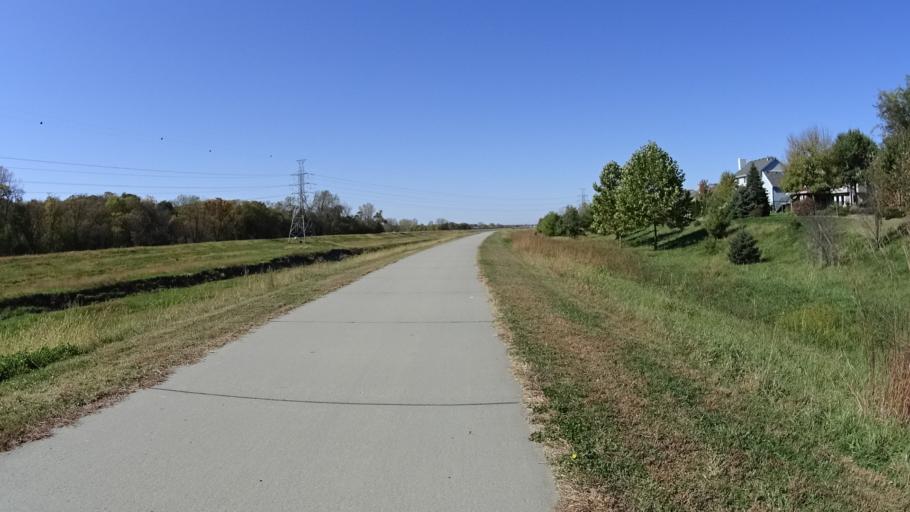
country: US
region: Nebraska
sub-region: Sarpy County
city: Papillion
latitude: 41.1508
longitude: -96.0057
